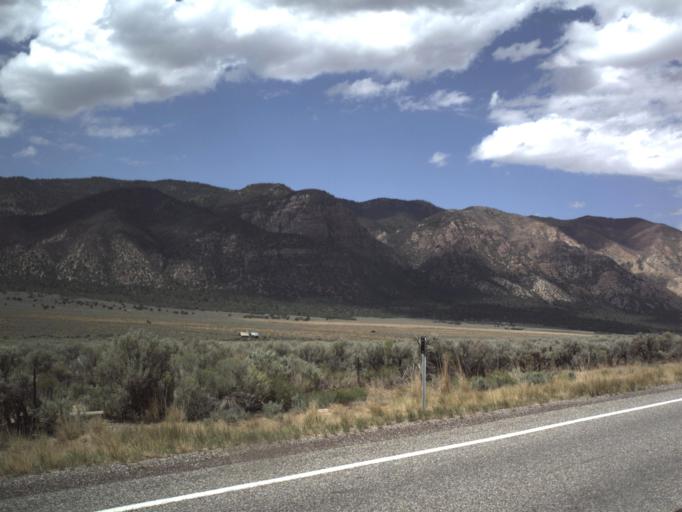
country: US
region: Utah
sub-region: Sevier County
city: Aurora
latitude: 39.1204
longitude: -112.0494
